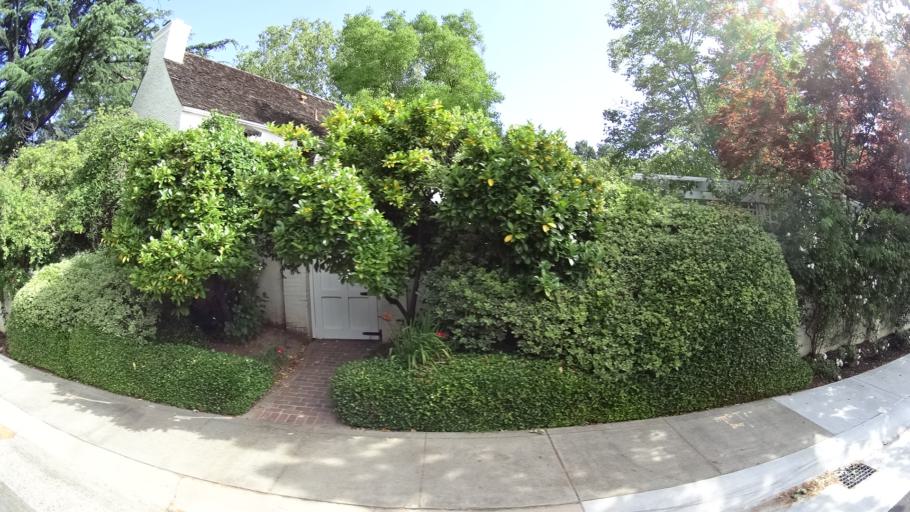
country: US
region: California
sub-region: Sacramento County
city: Sacramento
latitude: 38.5442
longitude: -121.4924
